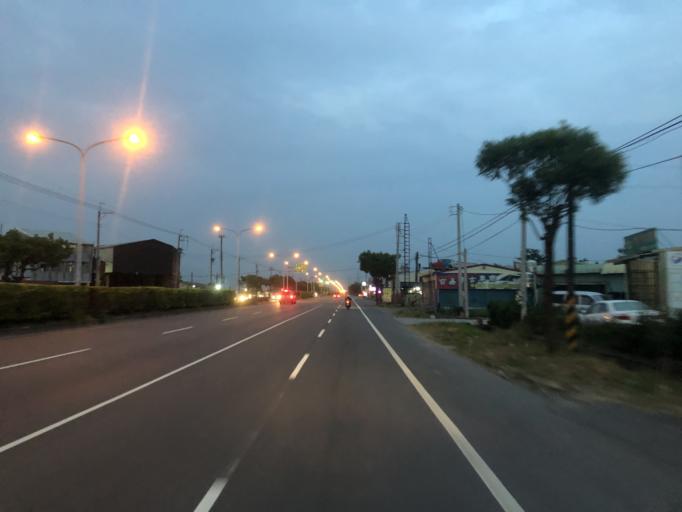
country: TW
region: Taiwan
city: Yujing
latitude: 23.1427
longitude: 120.3258
